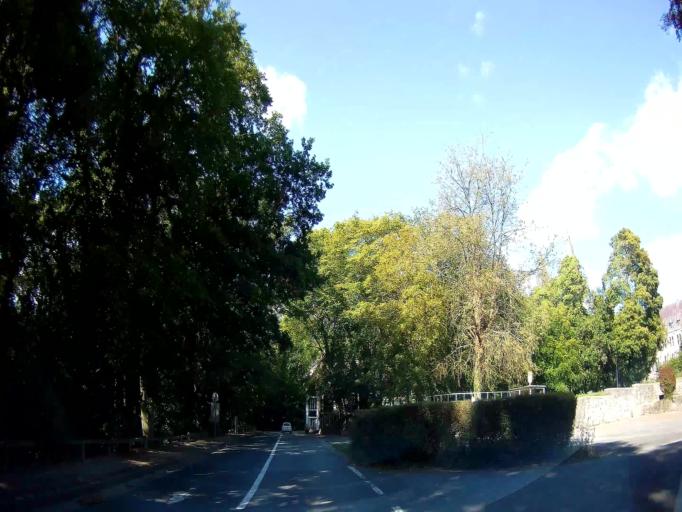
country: BE
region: Wallonia
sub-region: Province de Namur
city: Onhaye
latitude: 50.3017
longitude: 4.7647
